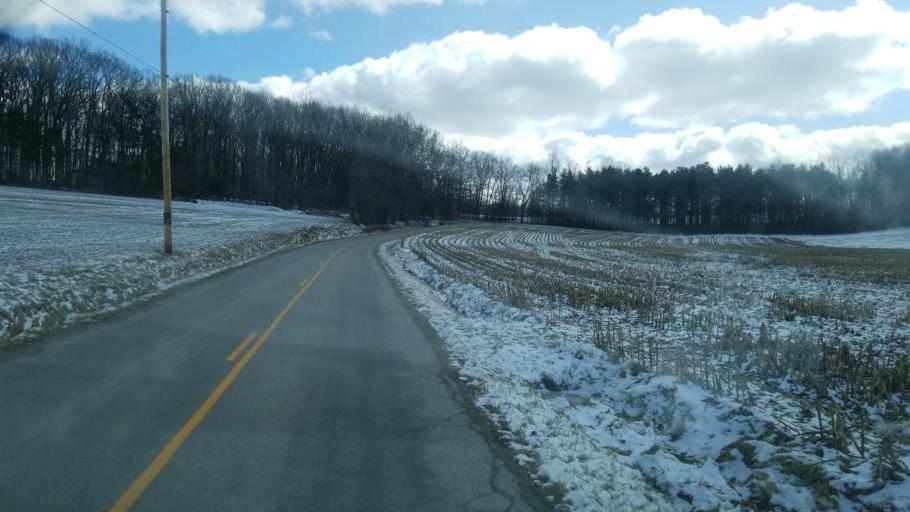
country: US
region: Ohio
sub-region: Ashland County
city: Loudonville
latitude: 40.5895
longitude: -82.3688
